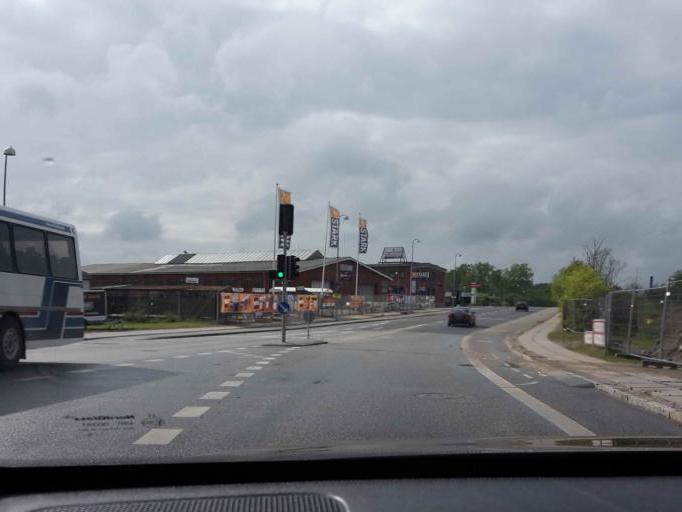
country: DK
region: South Denmark
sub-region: Odense Kommune
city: Odense
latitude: 55.4029
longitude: 10.3786
